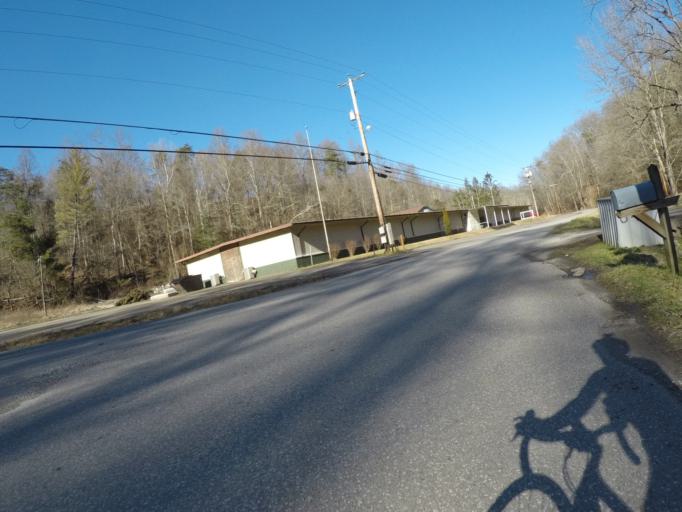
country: US
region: Kentucky
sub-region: Boyd County
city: Catlettsburg
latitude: 38.4209
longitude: -82.6392
